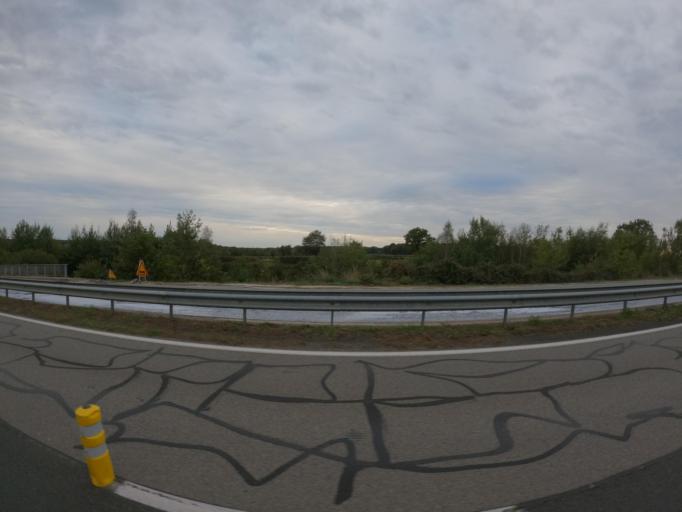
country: FR
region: Poitou-Charentes
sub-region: Departement des Deux-Sevres
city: La Peyratte
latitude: 46.6524
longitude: -0.1244
